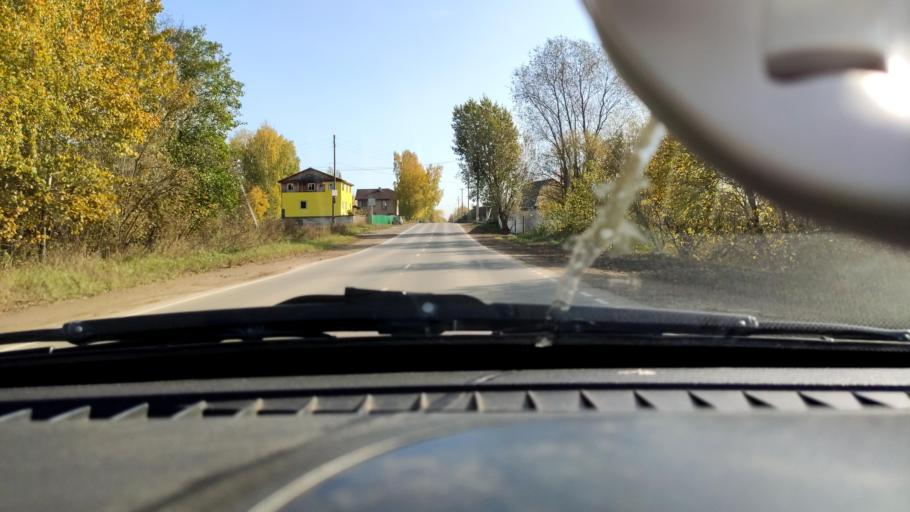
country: RU
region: Perm
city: Overyata
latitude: 58.0568
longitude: 55.8611
